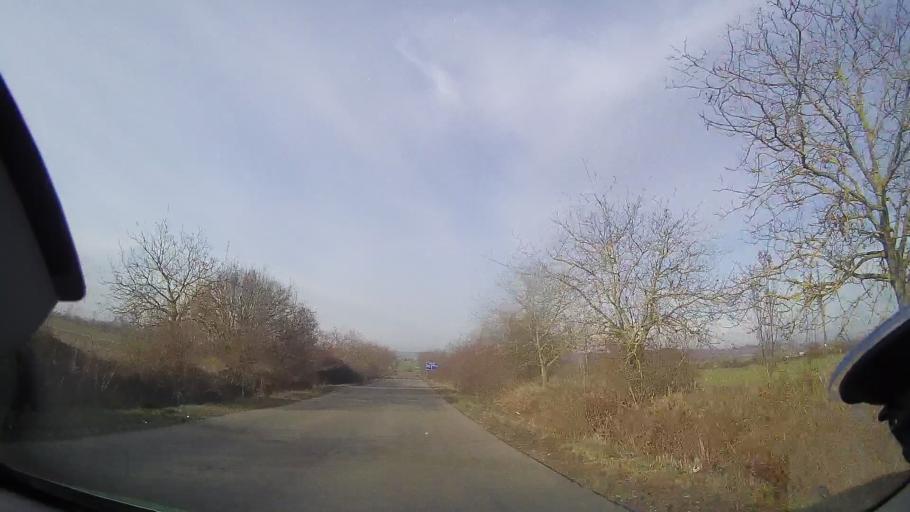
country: RO
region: Bihor
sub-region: Comuna Spinus
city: Spinus
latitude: 47.2252
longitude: 22.1684
